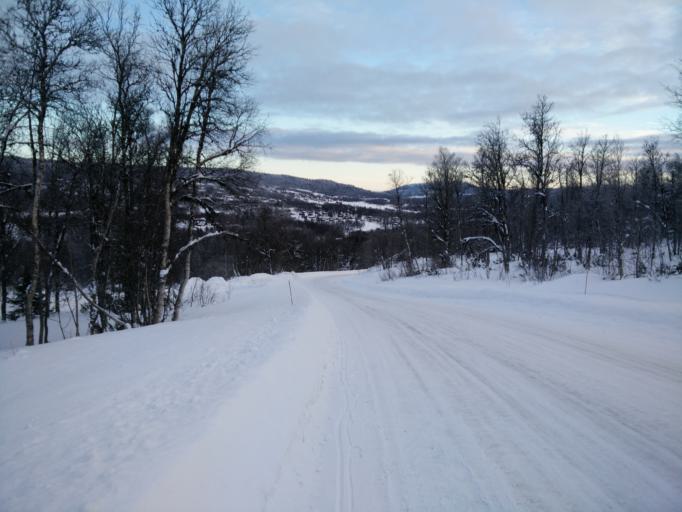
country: NO
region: Sor-Trondelag
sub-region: Tydal
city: Aas
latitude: 62.6514
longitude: 12.4101
